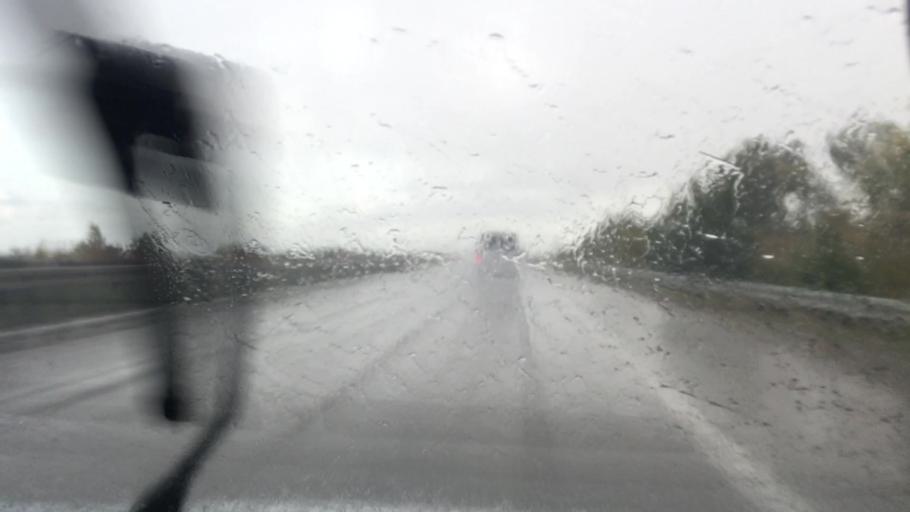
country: DE
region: Saxony-Anhalt
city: Eickendorf
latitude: 51.9642
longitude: 11.6754
